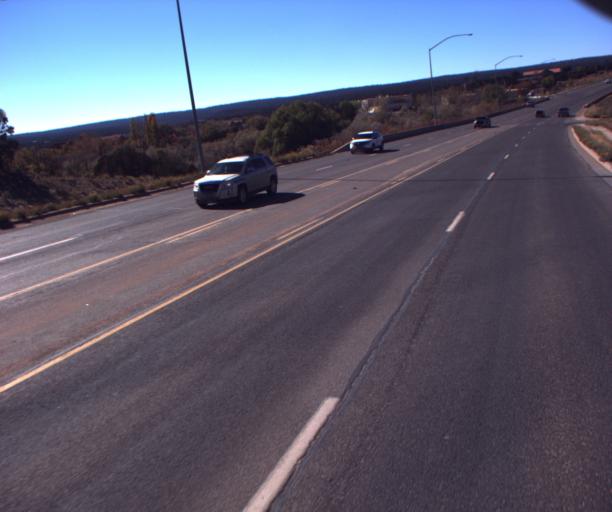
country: US
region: Arizona
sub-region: Apache County
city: Saint Michaels
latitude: 35.6552
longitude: -109.1020
